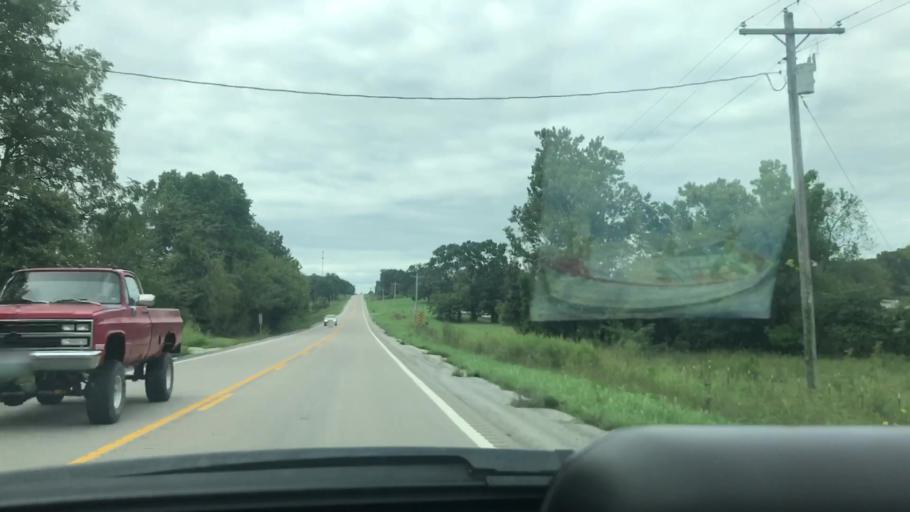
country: US
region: Missouri
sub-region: Benton County
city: Warsaw
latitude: 38.1347
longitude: -93.2818
